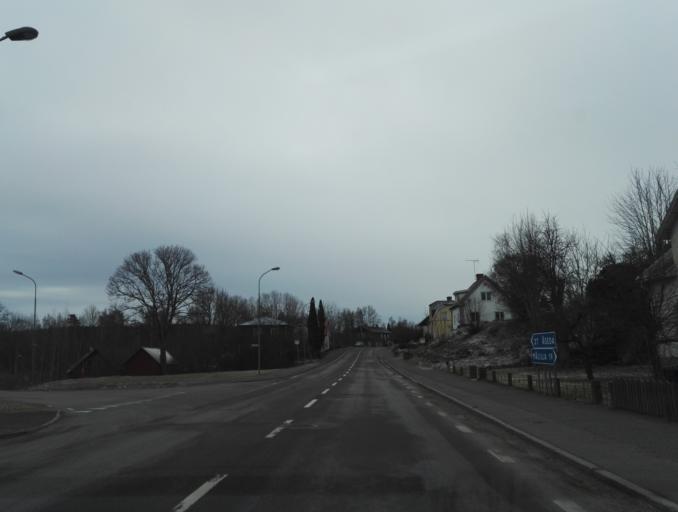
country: SE
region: Kalmar
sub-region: Hultsfreds Kommun
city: Virserum
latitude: 57.3112
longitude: 15.5850
